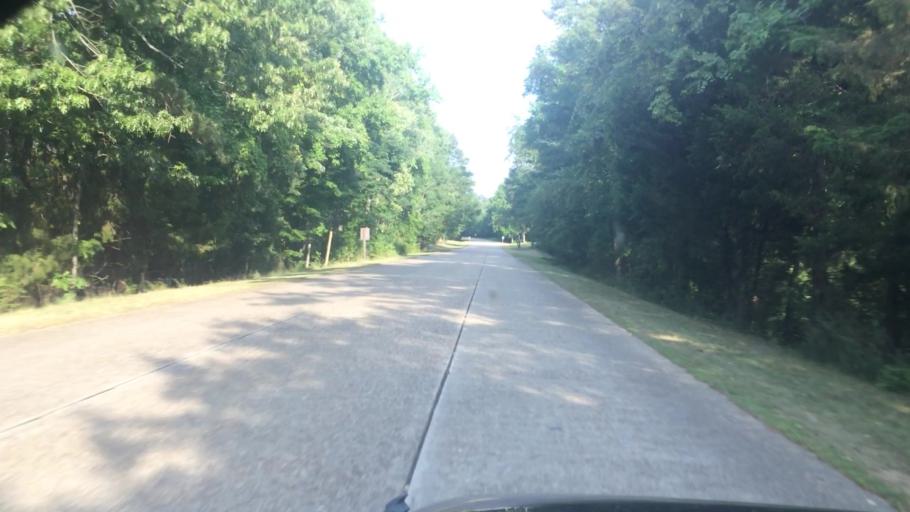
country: US
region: Virginia
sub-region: James City County
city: Williamsburg
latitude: 37.2232
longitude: -76.7765
